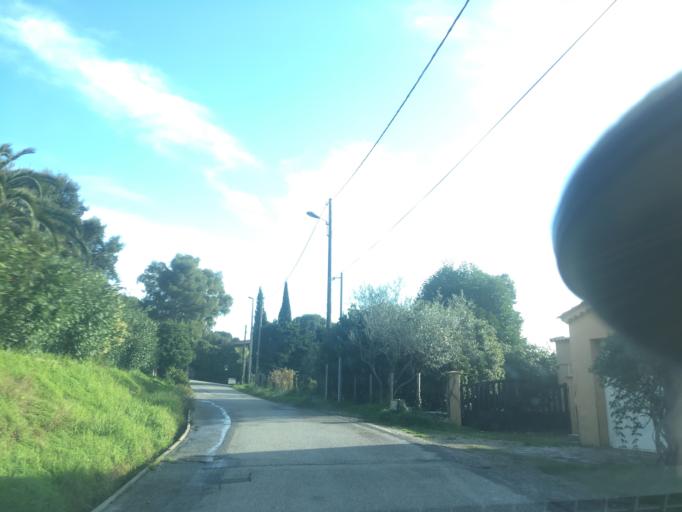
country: FR
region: Provence-Alpes-Cote d'Azur
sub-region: Departement du Var
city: Cavalaire-sur-Mer
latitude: 43.1582
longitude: 6.4765
